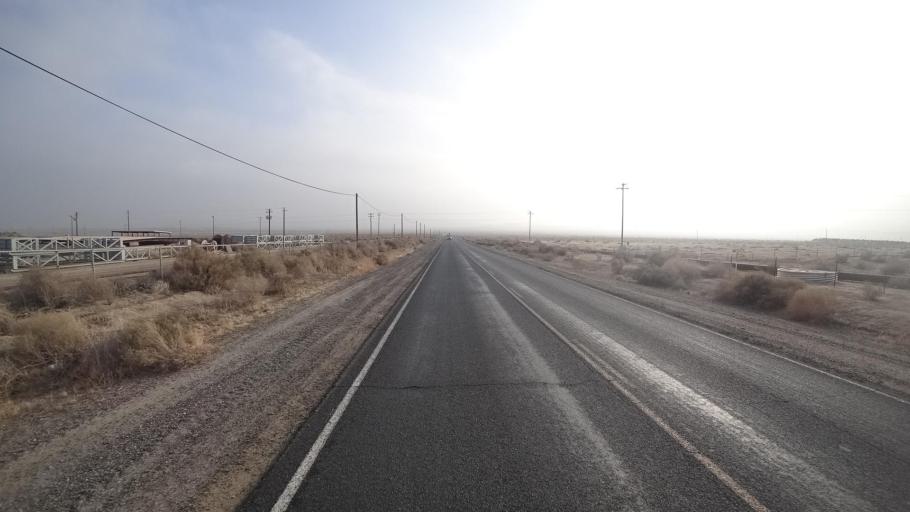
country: US
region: California
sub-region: Kern County
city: Ford City
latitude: 35.2319
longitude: -119.4456
